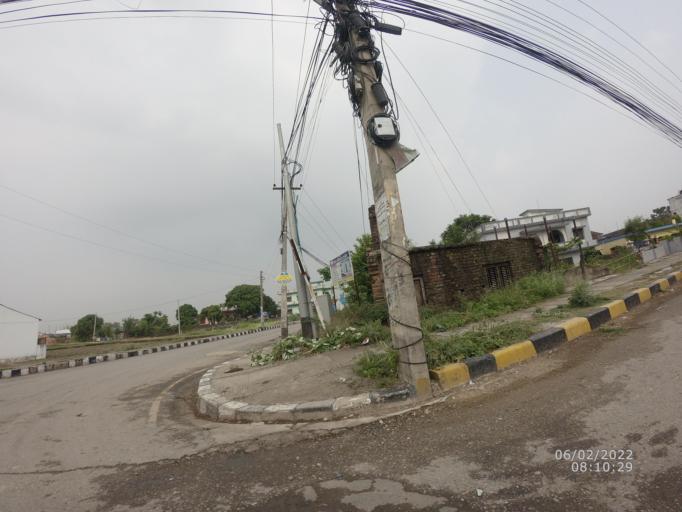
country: NP
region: Western Region
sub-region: Lumbini Zone
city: Bhairahawa
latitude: 27.4926
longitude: 83.4601
